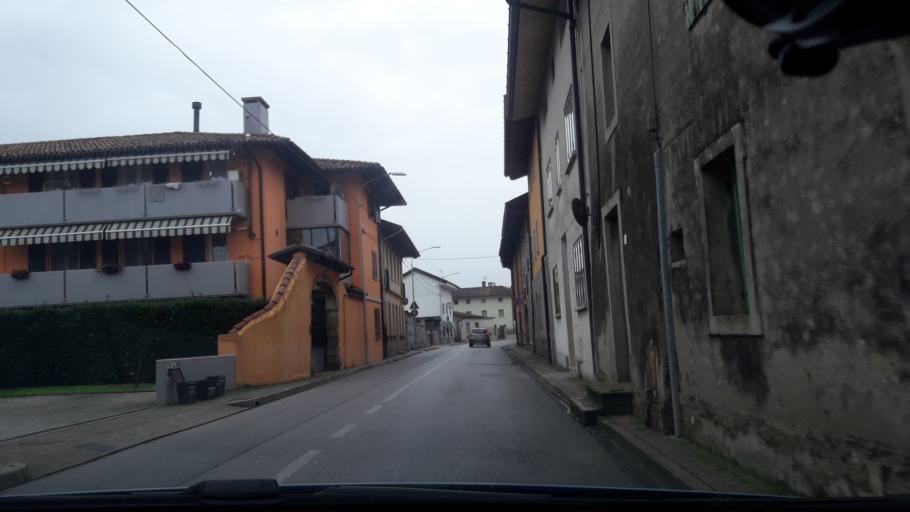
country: IT
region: Friuli Venezia Giulia
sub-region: Provincia di Udine
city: Colloredo di Prato
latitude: 46.0513
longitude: 13.1430
